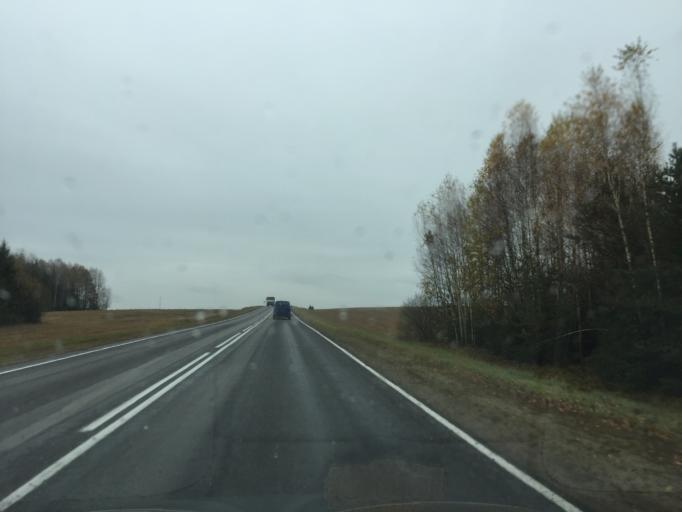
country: BY
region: Mogilev
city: Cherykaw
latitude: 53.6664
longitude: 31.2296
